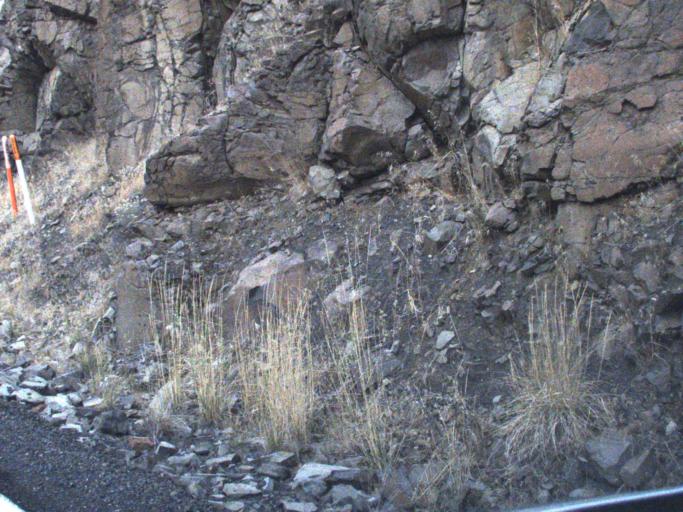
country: US
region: Washington
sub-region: Garfield County
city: Pomeroy
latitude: 46.4418
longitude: -117.3820
